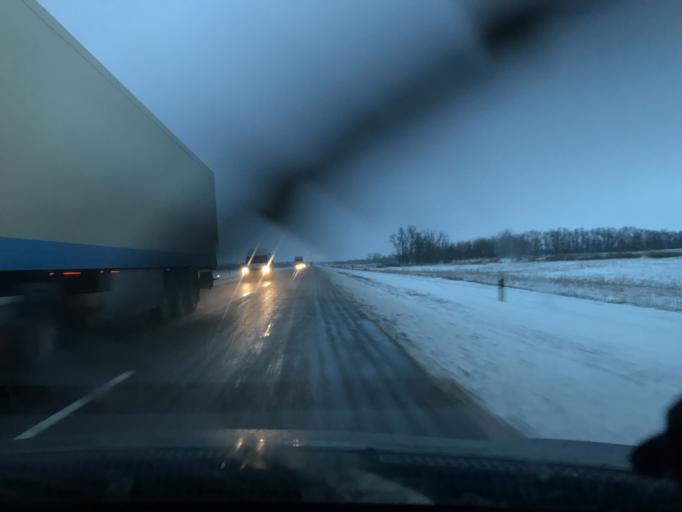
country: RU
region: Rostov
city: Letnik
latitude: 45.9796
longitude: 41.2431
